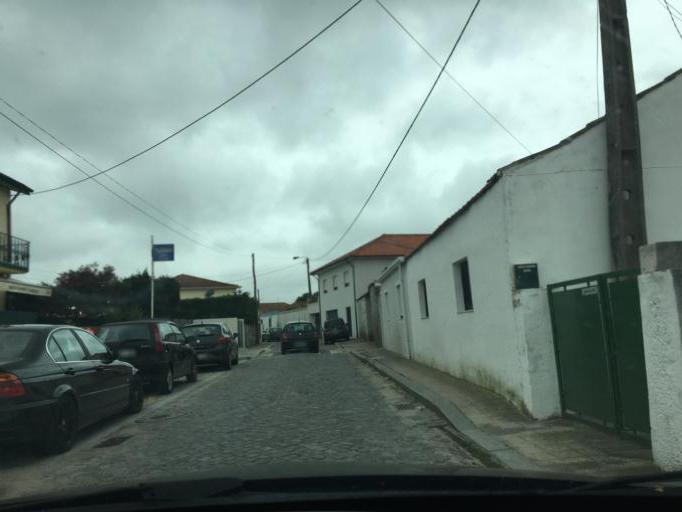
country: PT
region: Porto
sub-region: Matosinhos
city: Santa Cruz do Bispo
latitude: 41.2251
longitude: -8.6781
